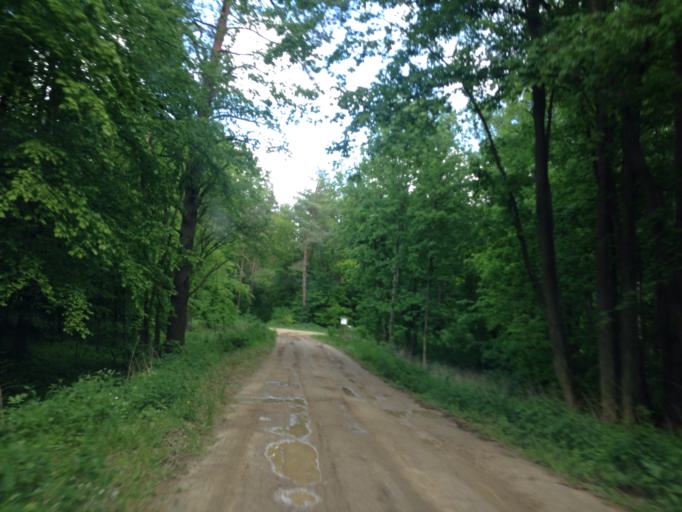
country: PL
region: Warmian-Masurian Voivodeship
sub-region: Powiat nidzicki
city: Nidzica
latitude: 53.4644
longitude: 20.3627
